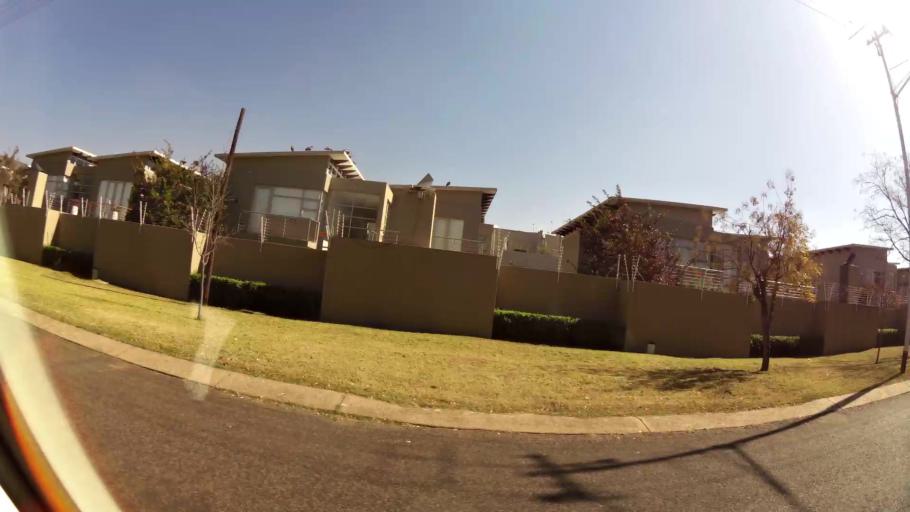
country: ZA
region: Gauteng
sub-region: City of Tshwane Metropolitan Municipality
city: Pretoria
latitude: -25.7711
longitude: 28.2374
